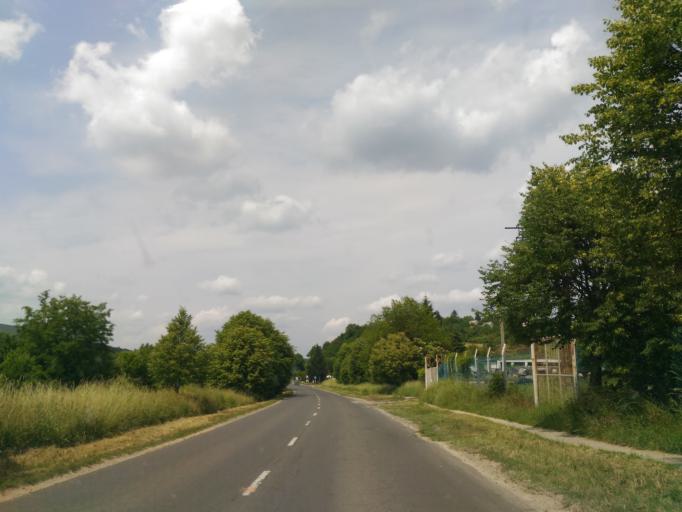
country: HU
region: Baranya
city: Komlo
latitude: 46.1998
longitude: 18.2520
